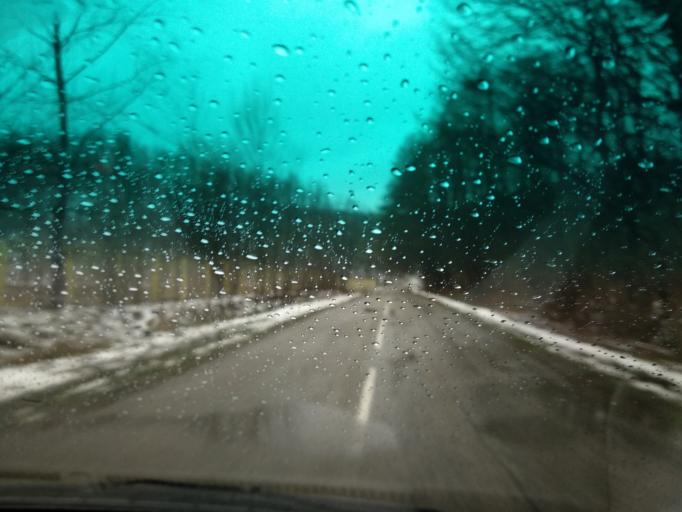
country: RU
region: Krasnodarskiy
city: Khadyzhensk
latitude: 44.2208
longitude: 39.3916
